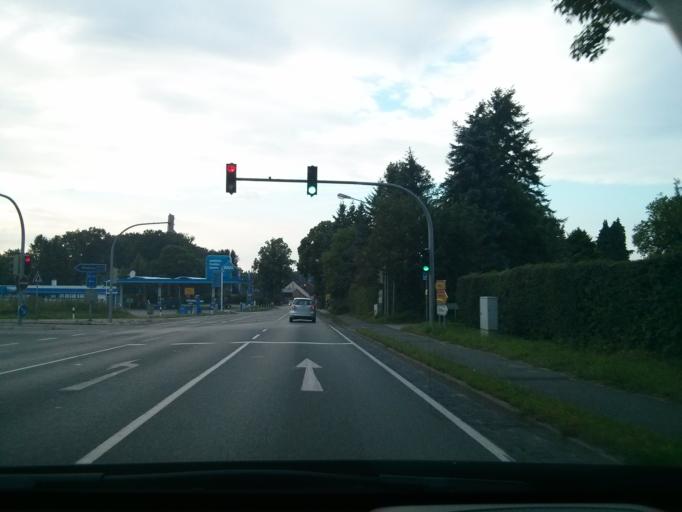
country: DE
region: Lower Saxony
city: Seevetal
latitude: 53.3814
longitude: 9.9804
